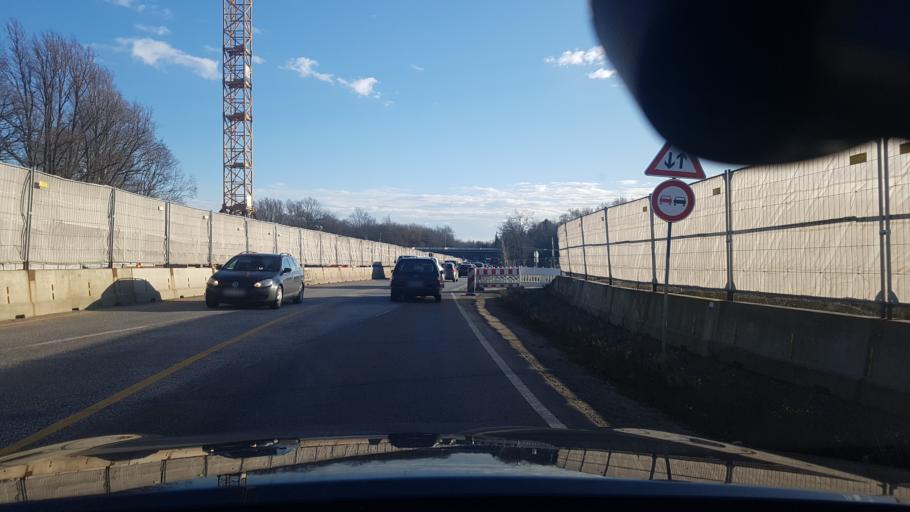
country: DE
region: Lower Saxony
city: Langen
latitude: 53.5839
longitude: 8.6114
